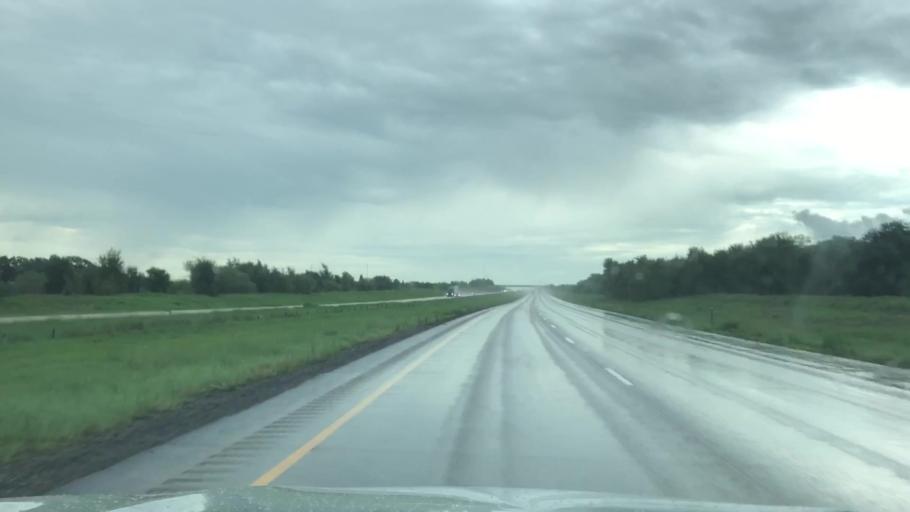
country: US
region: Texas
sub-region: Fayette County
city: Flatonia
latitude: 29.6966
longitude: -97.1386
